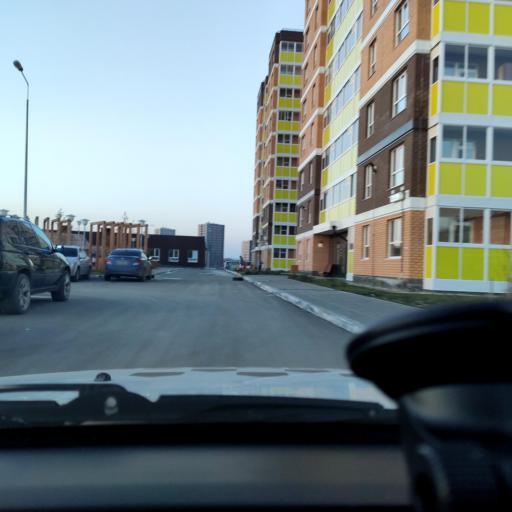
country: RU
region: Perm
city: Perm
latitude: 58.0042
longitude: 56.3340
